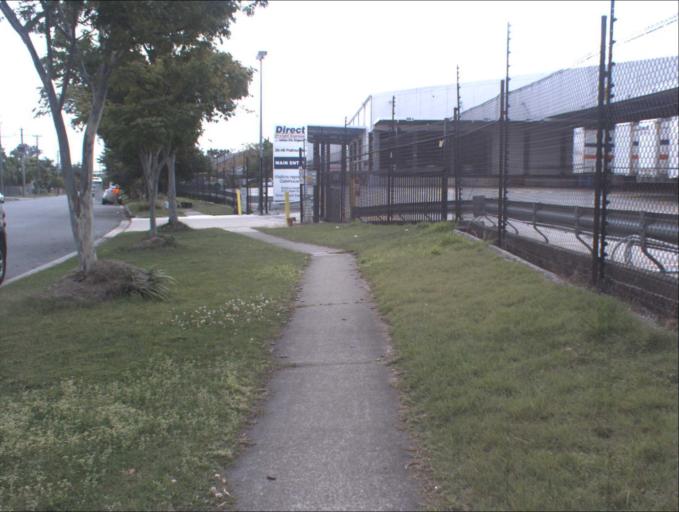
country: AU
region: Queensland
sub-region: Logan
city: Logan Reserve
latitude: -27.6825
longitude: 153.0762
